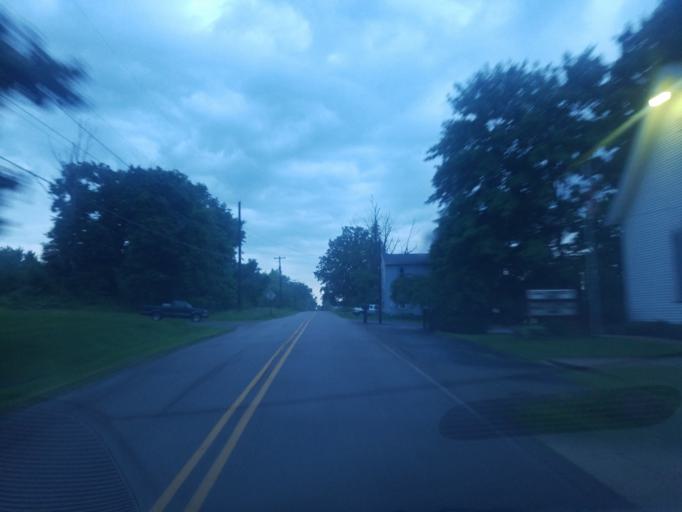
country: US
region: Ohio
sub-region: Mahoning County
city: Canfield
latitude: 40.9727
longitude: -80.7730
